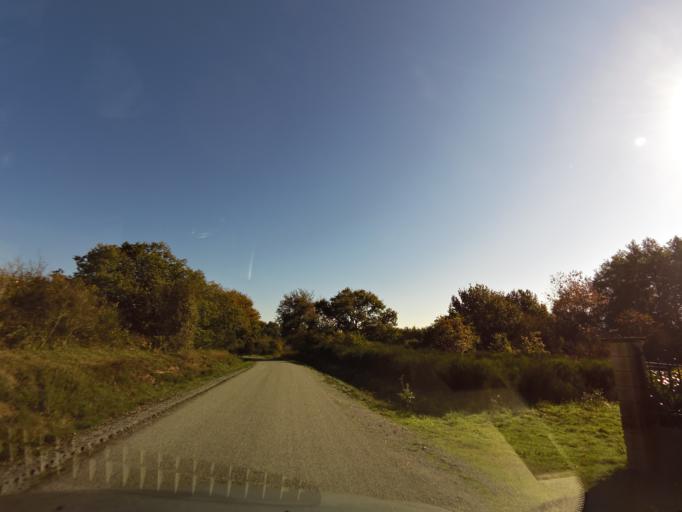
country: FR
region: Brittany
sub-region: Departement d'Ille-et-Vilaine
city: Bain-de-Bretagne
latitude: 47.8628
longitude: -1.7027
